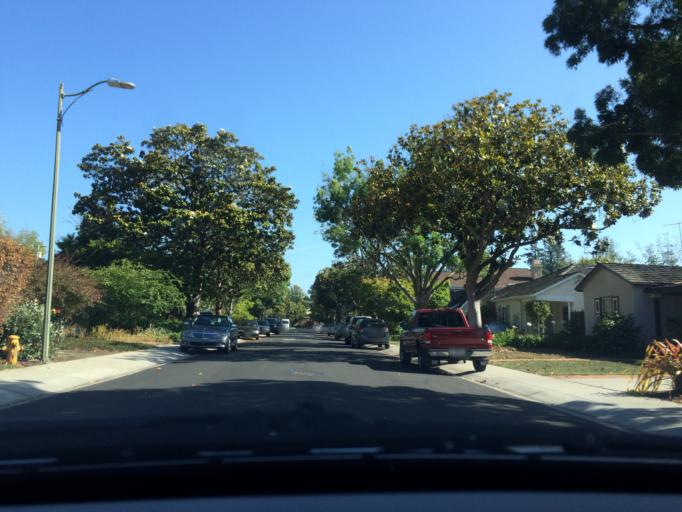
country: US
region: California
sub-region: Santa Clara County
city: Palo Alto
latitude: 37.4468
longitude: -122.1335
